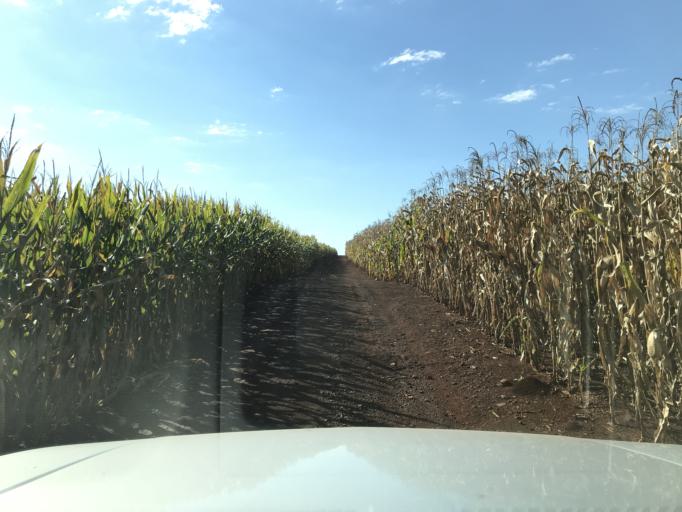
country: BR
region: Parana
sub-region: Palotina
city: Palotina
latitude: -24.2638
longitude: -53.8131
